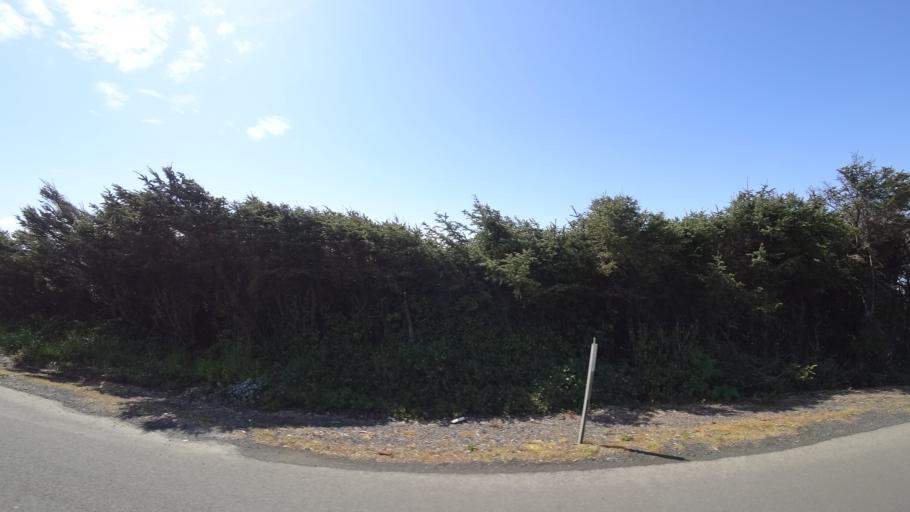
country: US
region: Oregon
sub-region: Lincoln County
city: Newport
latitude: 44.7026
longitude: -124.0611
